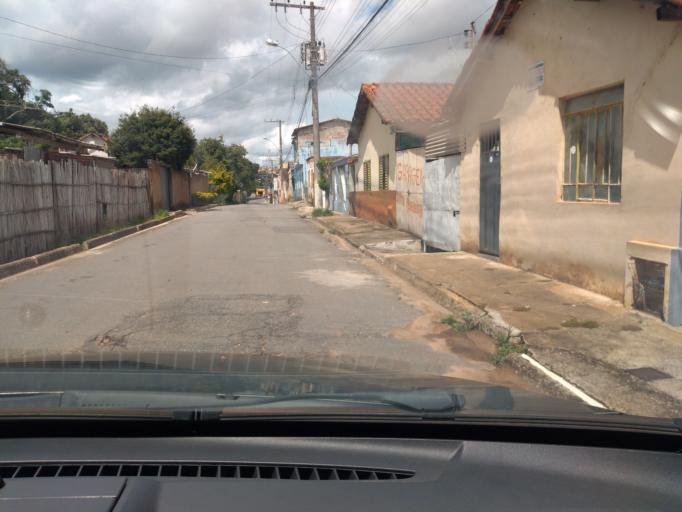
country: BR
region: Minas Gerais
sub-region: Tres Coracoes
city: Tres Coracoes
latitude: -21.6976
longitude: -45.2650
